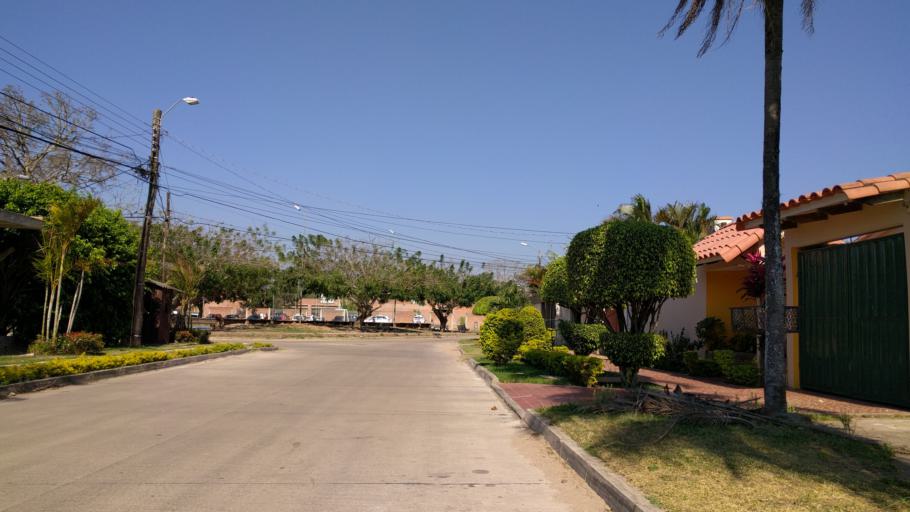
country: BO
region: Santa Cruz
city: Santa Cruz de la Sierra
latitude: -17.8101
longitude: -63.2260
